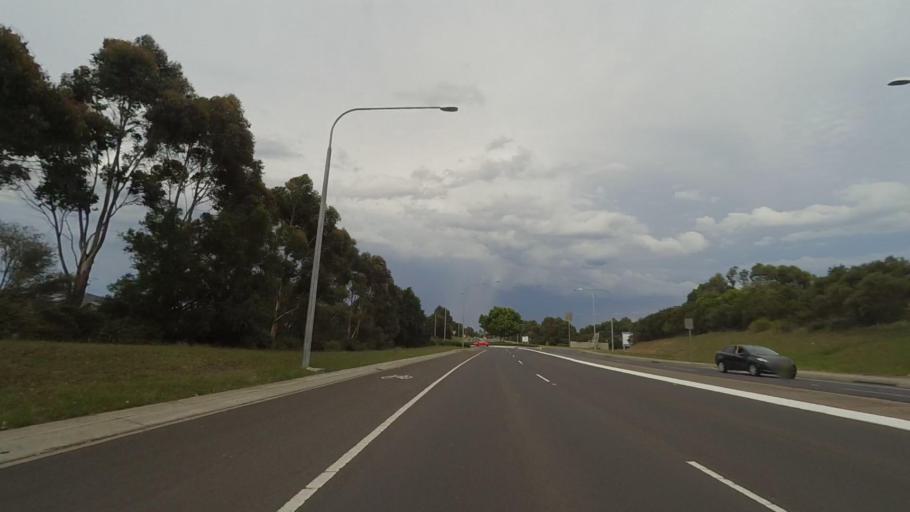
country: AU
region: New South Wales
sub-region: Shellharbour
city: Flinders
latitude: -34.5889
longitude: 150.8523
